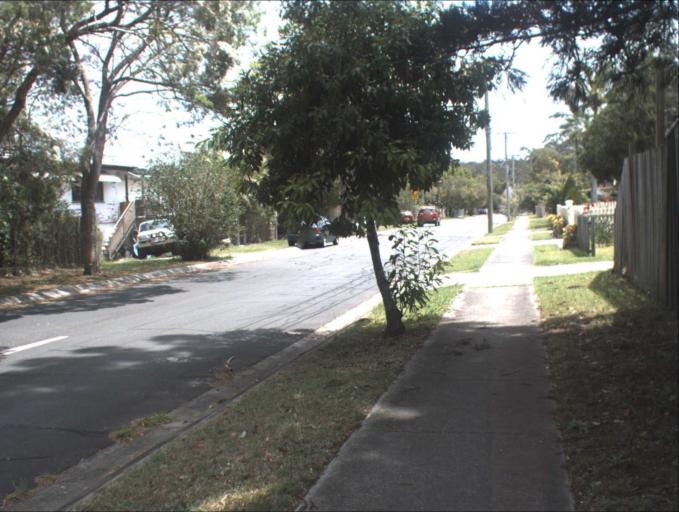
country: AU
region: Queensland
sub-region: Logan
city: Woodridge
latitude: -27.6383
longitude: 153.0980
